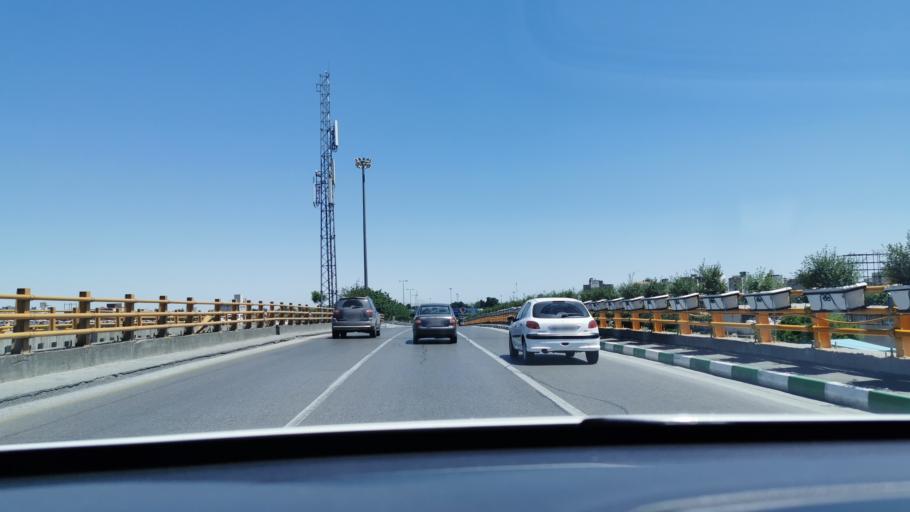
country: IR
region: Razavi Khorasan
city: Mashhad
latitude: 36.2559
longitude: 59.5986
